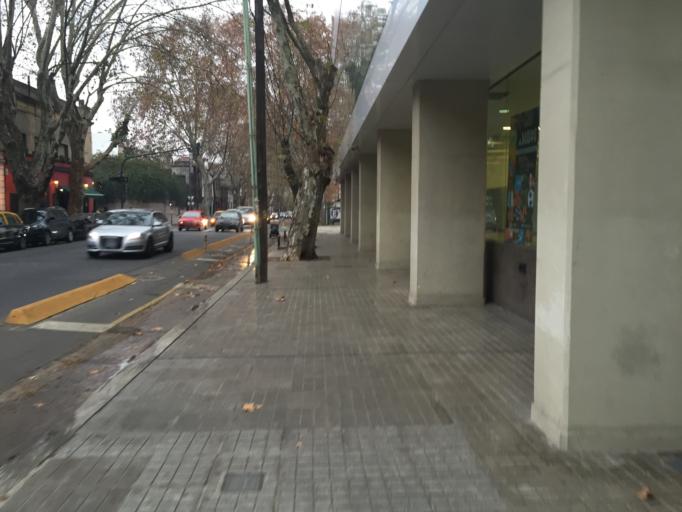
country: AR
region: Buenos Aires F.D.
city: Colegiales
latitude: -34.5829
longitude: -58.4290
